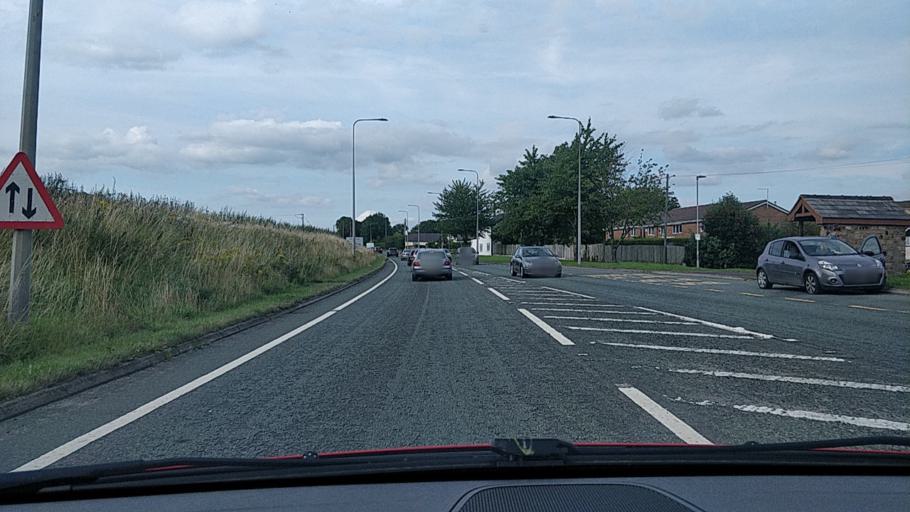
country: GB
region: Wales
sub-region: County of Flintshire
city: Penyffordd
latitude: 53.1546
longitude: -3.0438
